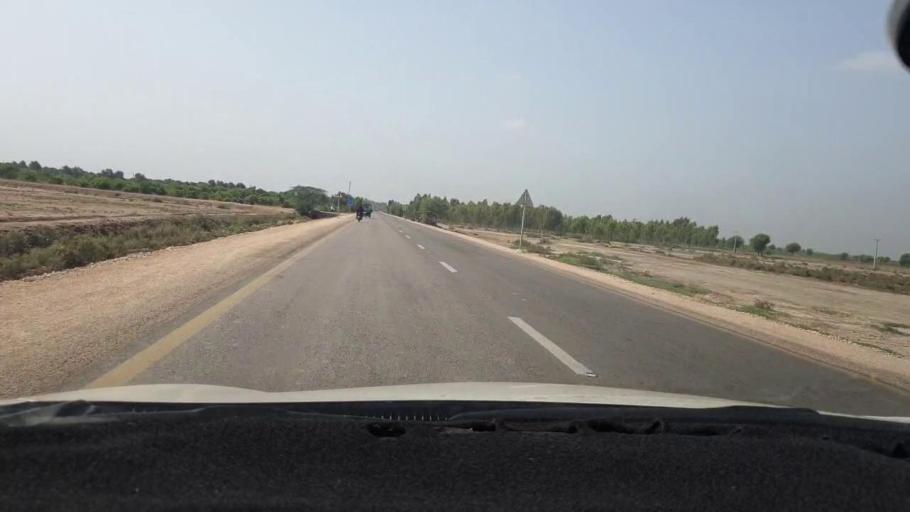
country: PK
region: Sindh
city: Mirpur Khas
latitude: 25.6732
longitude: 69.1068
